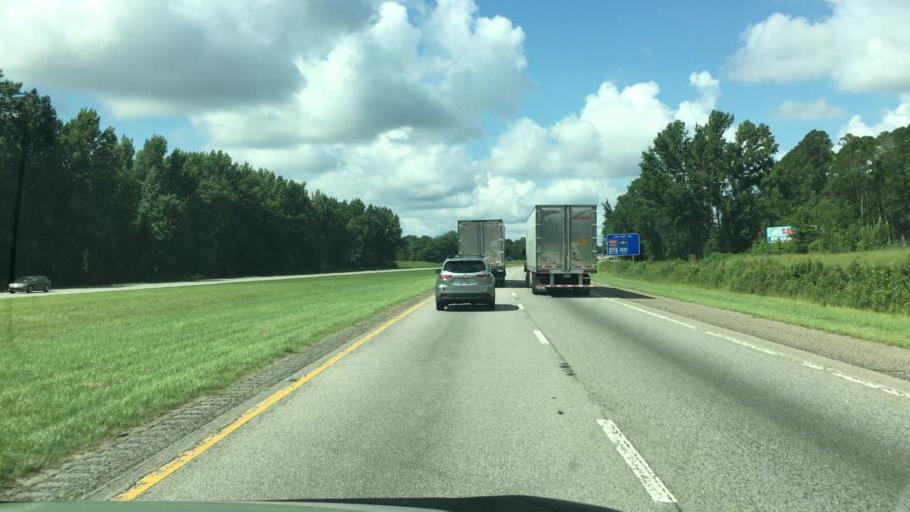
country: US
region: South Carolina
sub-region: Dillon County
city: Dillon
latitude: 34.4486
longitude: -79.3626
